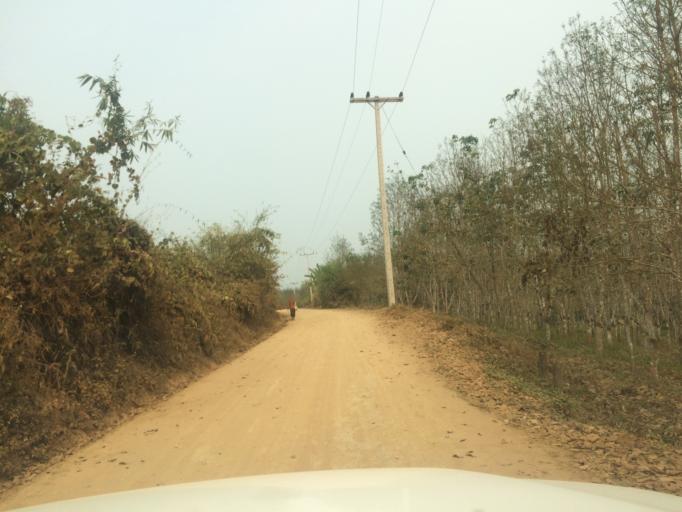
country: LA
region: Loungnamtha
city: Muang Nale
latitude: 20.4154
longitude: 101.6764
